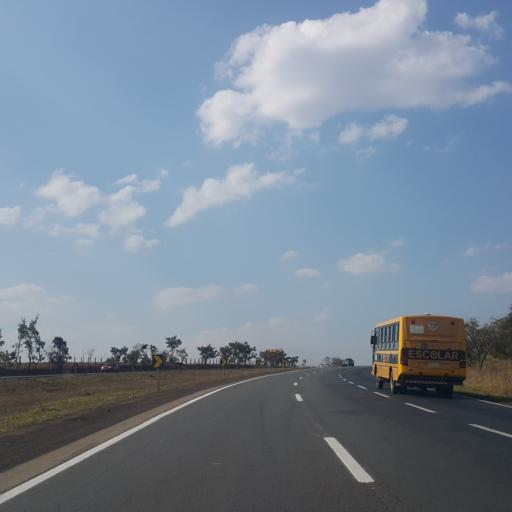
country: BR
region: Goias
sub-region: Abadiania
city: Abadiania
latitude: -16.2877
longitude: -48.7981
